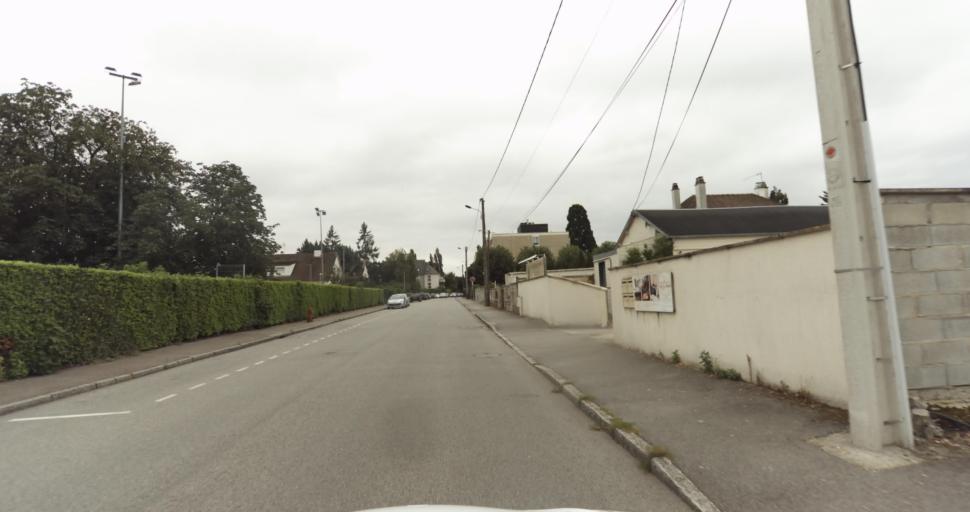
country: FR
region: Haute-Normandie
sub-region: Departement de l'Eure
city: Evreux
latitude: 49.0199
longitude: 1.1685
